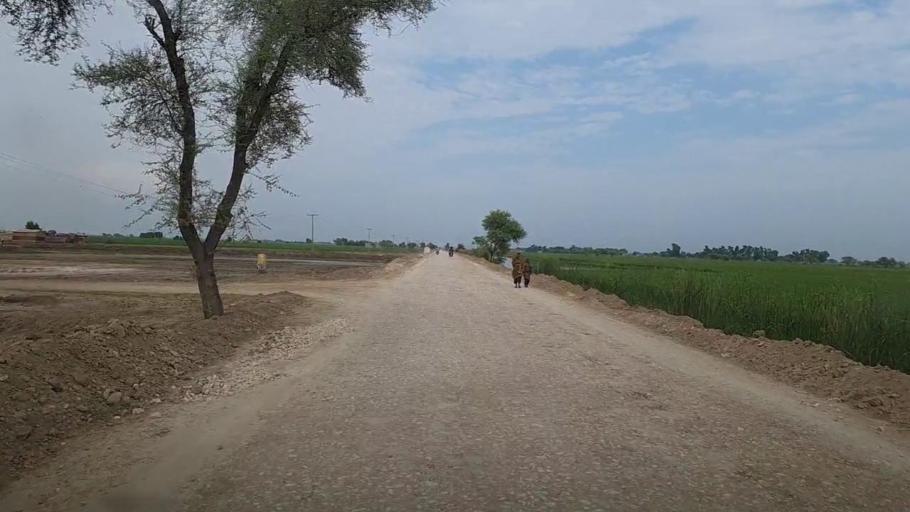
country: PK
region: Sindh
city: Thul
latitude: 28.2497
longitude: 68.7949
